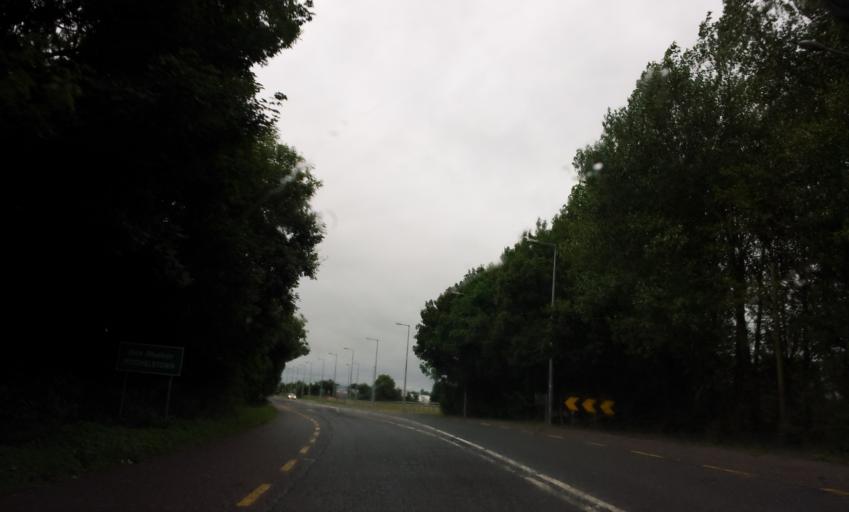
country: IE
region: Munster
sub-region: County Cork
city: Mitchelstown
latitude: 52.2764
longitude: -8.2644
